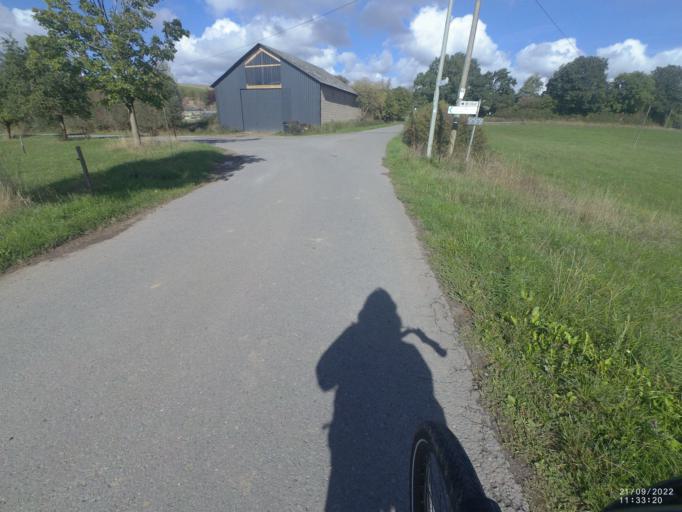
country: DE
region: Rheinland-Pfalz
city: Saxler
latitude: 50.1418
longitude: 6.8959
